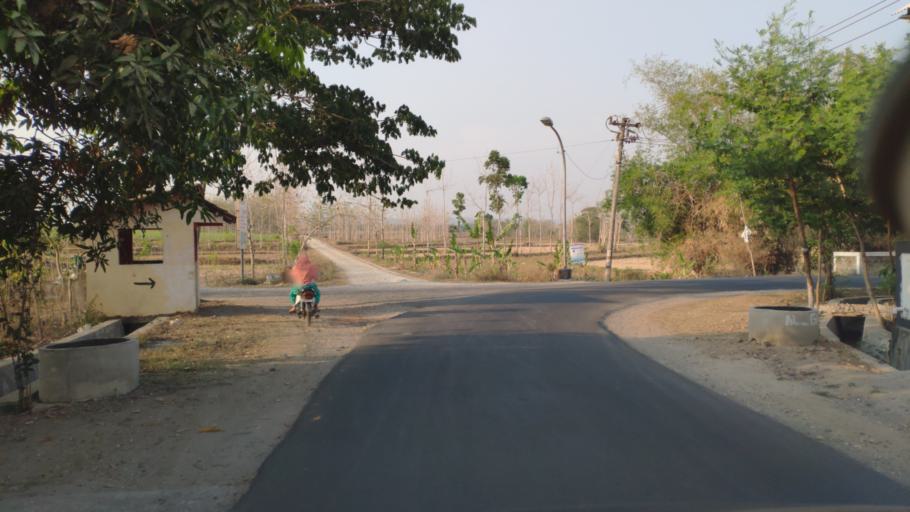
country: ID
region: Central Java
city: Jembangan
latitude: -6.9529
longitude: 111.3883
